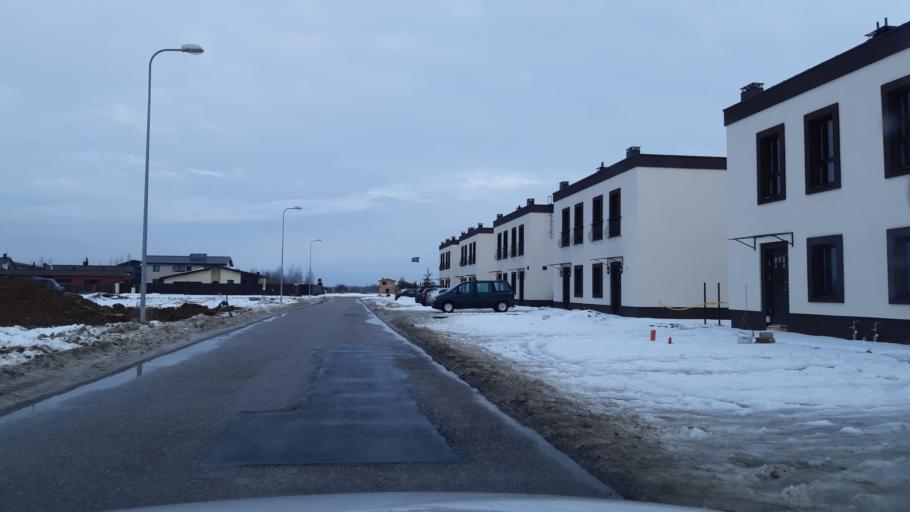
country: LT
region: Kauno apskritis
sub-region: Kauno rajonas
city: Garliava
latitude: 54.8396
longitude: 23.9024
